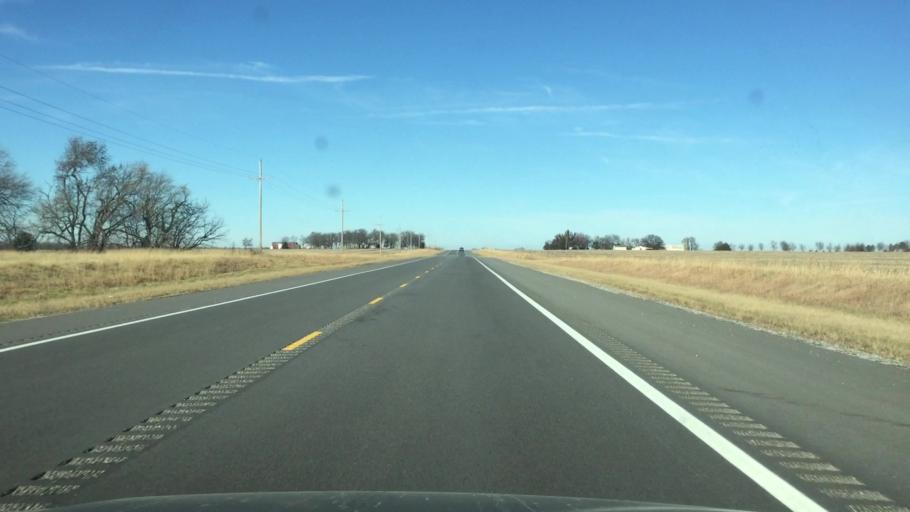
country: US
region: Kansas
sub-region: Franklin County
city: Ottawa
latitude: 38.5278
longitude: -95.2676
